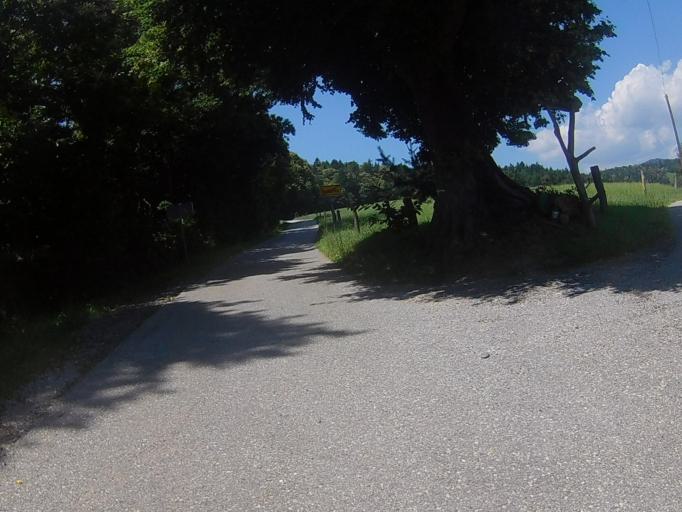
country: SI
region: Race-Fram
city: Fram
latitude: 46.4774
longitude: 15.6019
